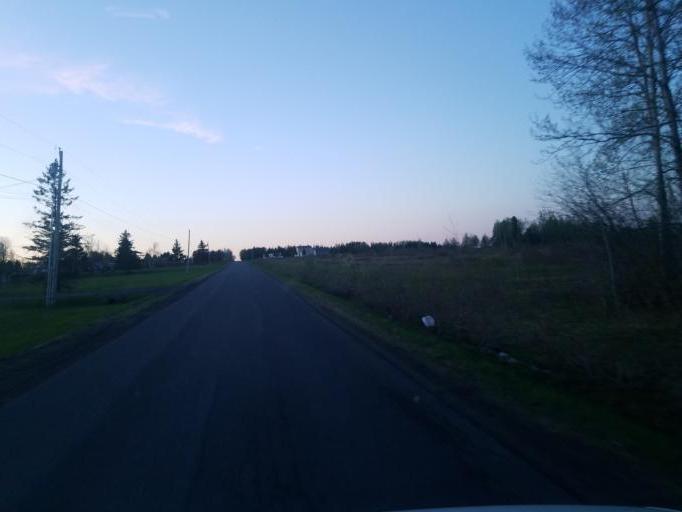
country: US
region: Maine
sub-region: Aroostook County
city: Caribou
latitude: 46.8464
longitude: -68.0704
